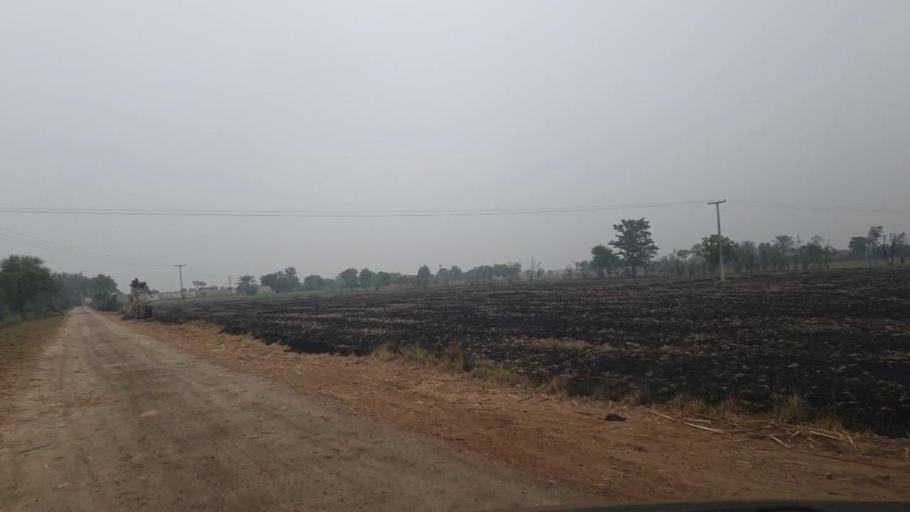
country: PK
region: Sindh
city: Tando Adam
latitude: 25.8027
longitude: 68.6845
